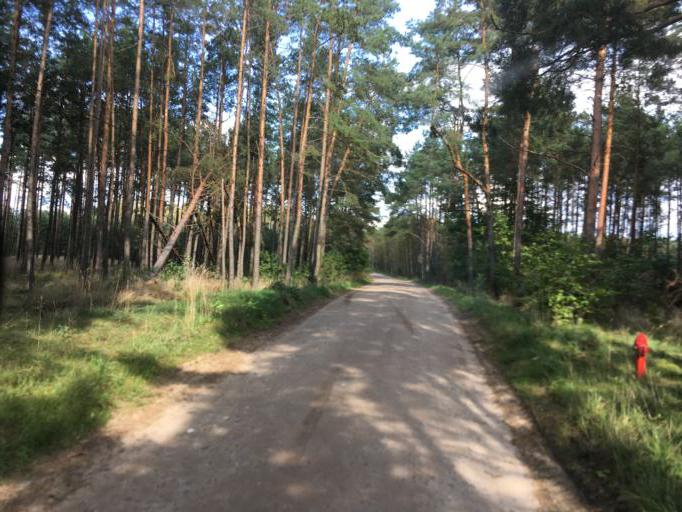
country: PL
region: Kujawsko-Pomorskie
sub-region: Powiat tucholski
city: Tuchola
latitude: 53.6040
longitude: 17.9104
